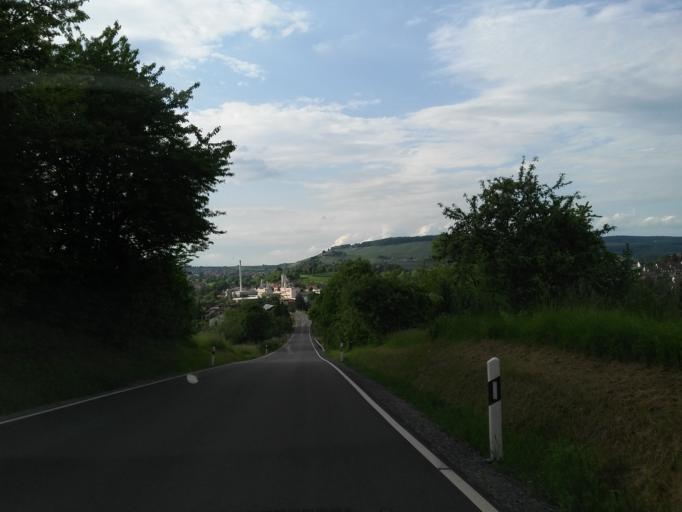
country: DE
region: Baden-Wuerttemberg
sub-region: Regierungsbezirk Stuttgart
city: Oberstenfeld
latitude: 49.0186
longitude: 9.3278
